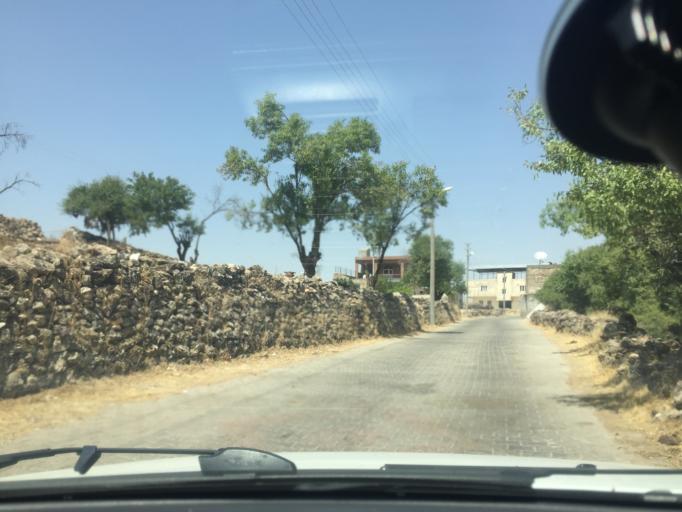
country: TR
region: Mardin
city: Kindirip
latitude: 37.4483
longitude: 41.2222
